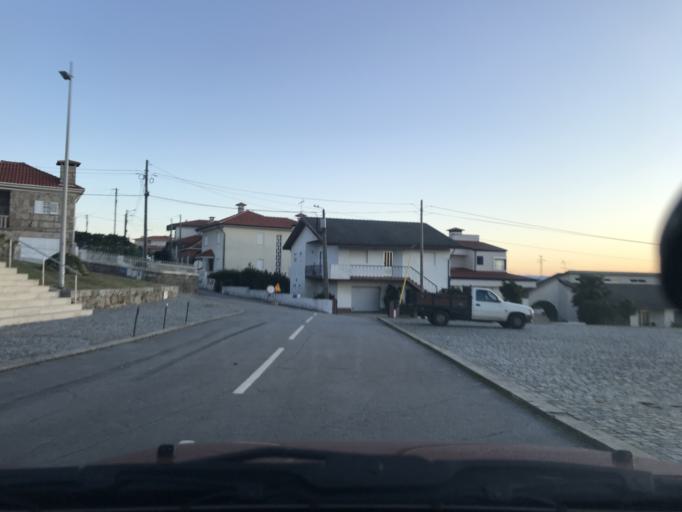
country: PT
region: Braga
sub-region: Vila Nova de Famalicao
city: Calendario
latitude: 41.3892
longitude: -8.5315
